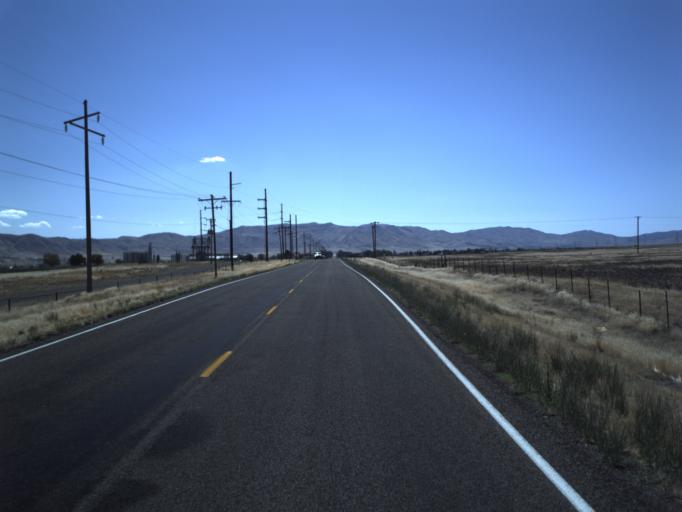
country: US
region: Utah
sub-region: Utah County
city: Genola
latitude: 39.9837
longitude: -111.9572
